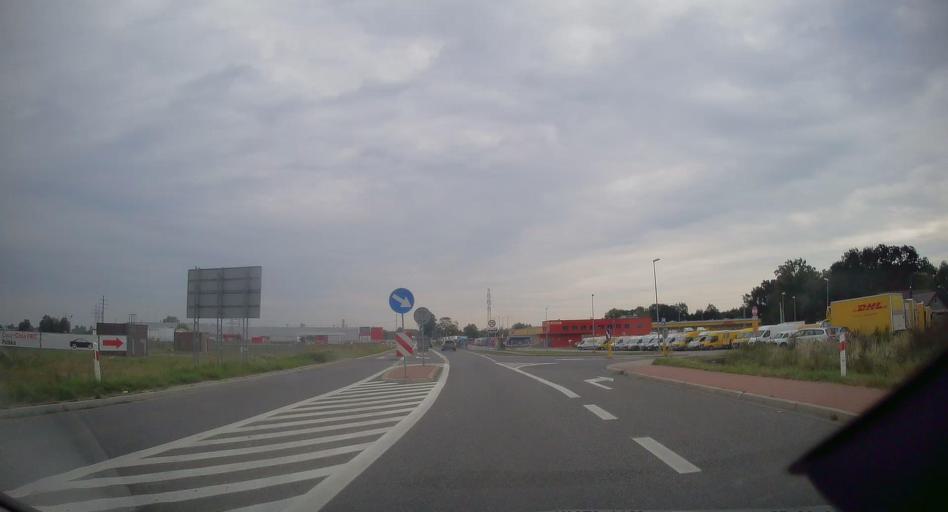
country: PL
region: Lesser Poland Voivodeship
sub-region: Powiat wielicki
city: Podleze
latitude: 50.0164
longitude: 20.1812
